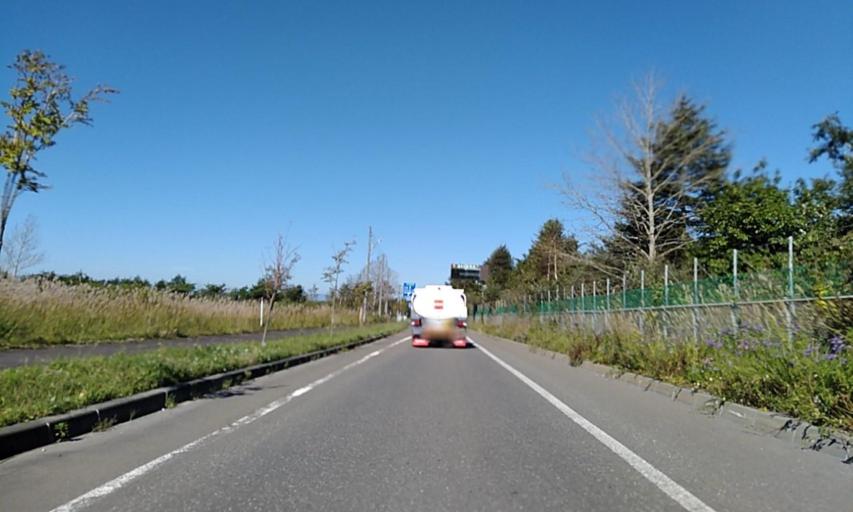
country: JP
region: Hokkaido
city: Tomakomai
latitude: 42.6914
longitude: 141.6911
